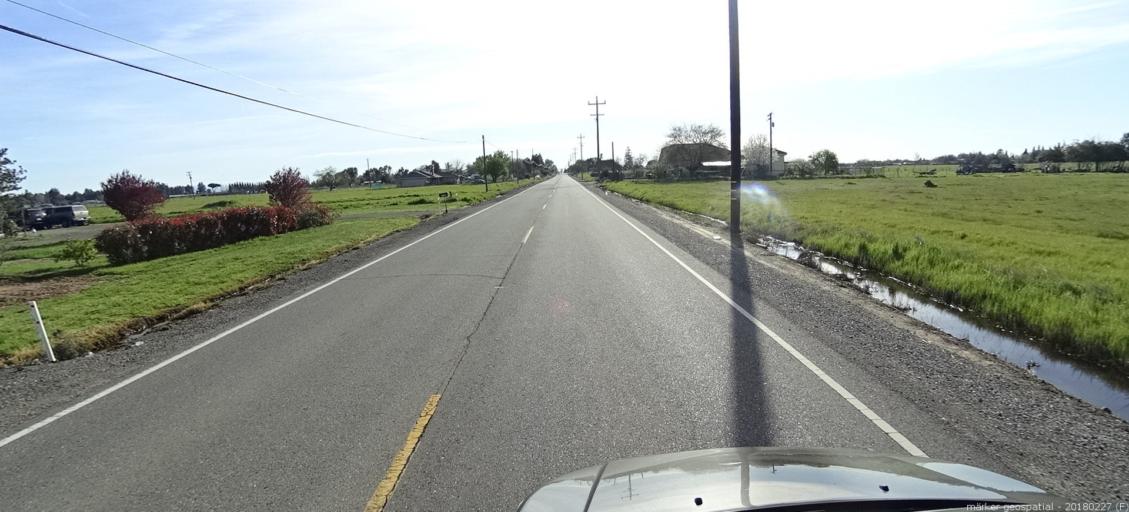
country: US
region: California
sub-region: Sacramento County
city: Vineyard
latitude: 38.4963
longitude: -121.3441
